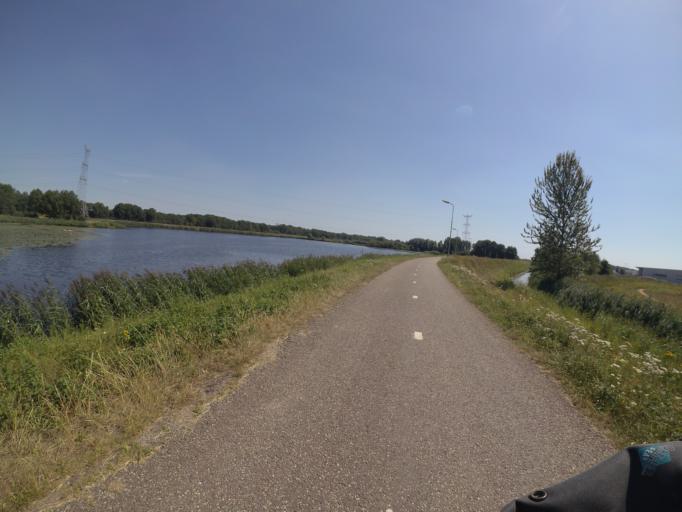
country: NL
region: North Brabant
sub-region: Gemeente 's-Hertogenbosch
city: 's-Hertogenbosch
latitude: 51.6934
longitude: 5.3532
